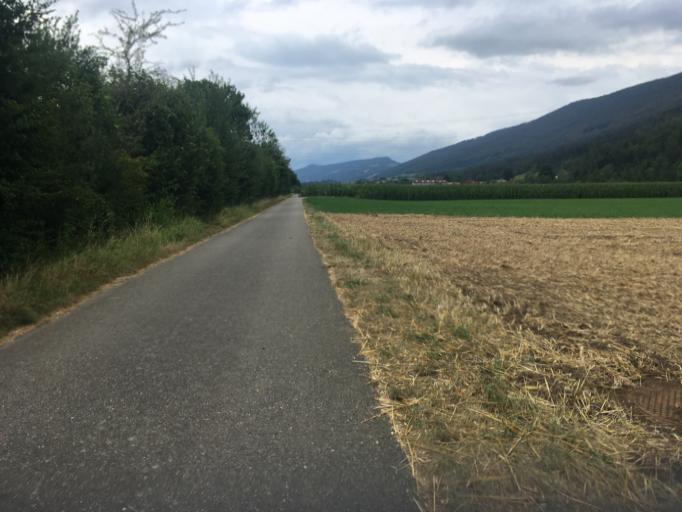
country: CH
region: Solothurn
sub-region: Bezirk Thal
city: Matzendorf
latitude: 47.2968
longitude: 7.6048
